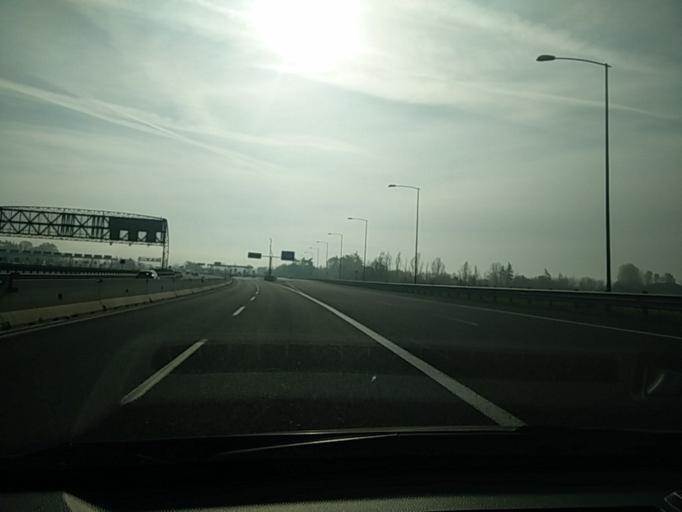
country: IT
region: Emilia-Romagna
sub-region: Provincia di Bologna
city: San Lazzaro
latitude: 44.4808
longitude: 11.4217
